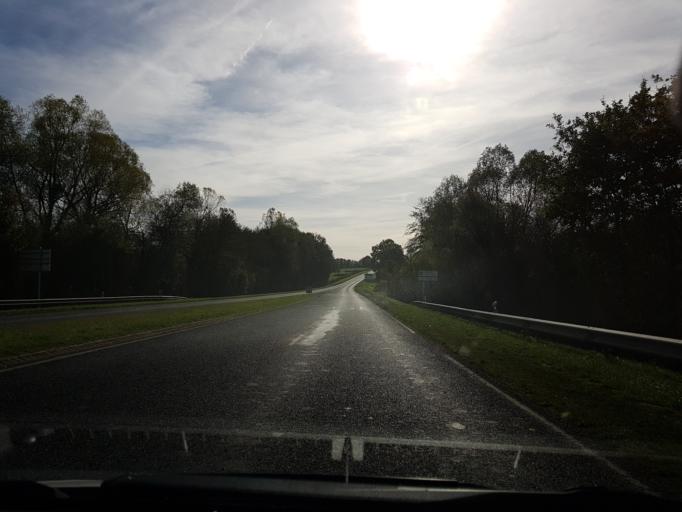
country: FR
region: Bourgogne
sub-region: Departement de l'Yonne
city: Avallon
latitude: 47.5018
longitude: 3.9921
